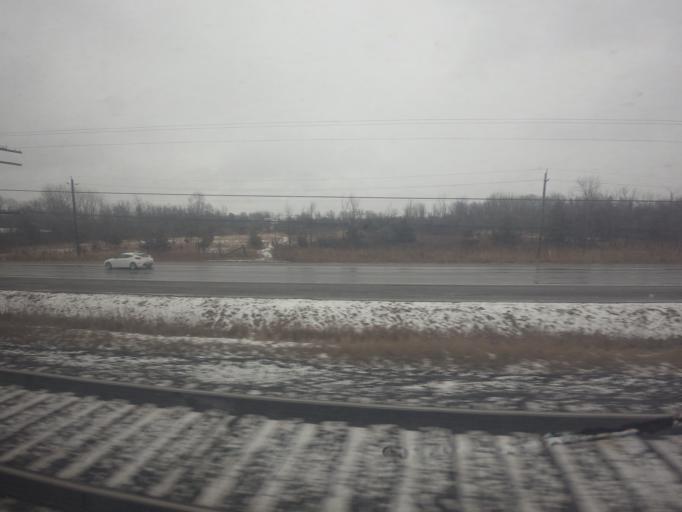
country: CA
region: Ontario
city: Belleville
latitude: 44.1673
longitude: -77.4146
